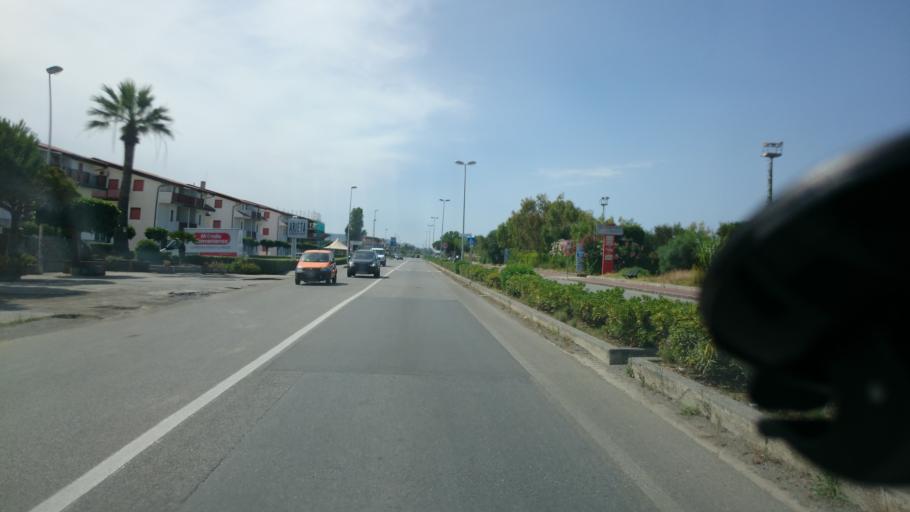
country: IT
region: Calabria
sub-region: Provincia di Cosenza
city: Scalea
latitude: 39.8020
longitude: 15.7911
